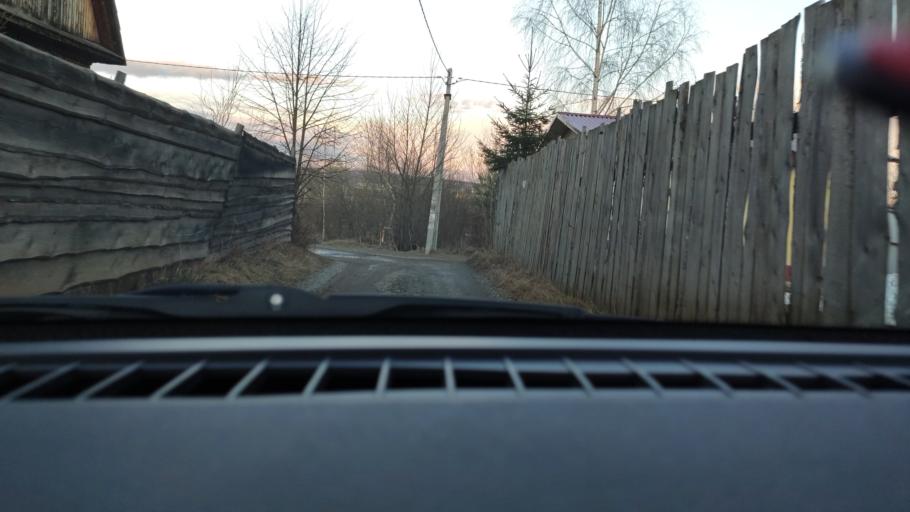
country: RU
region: Perm
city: Perm
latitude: 58.0824
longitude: 56.3186
